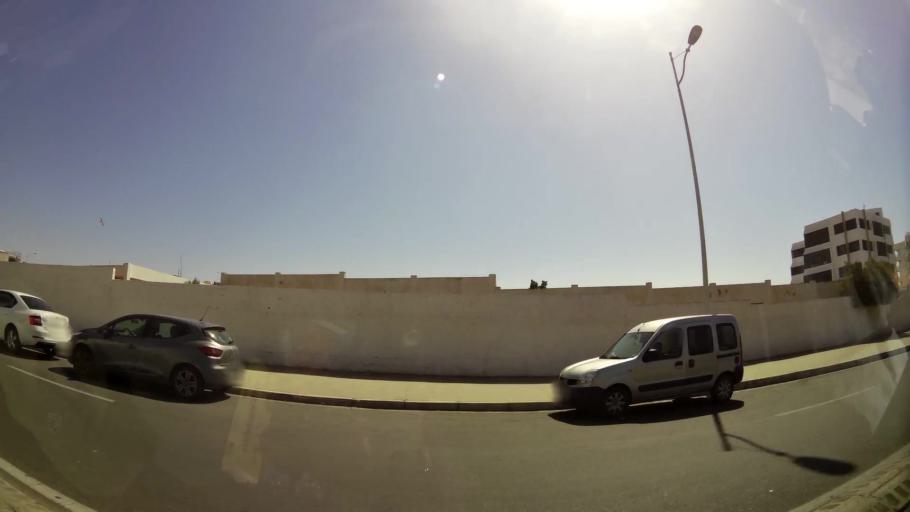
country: MA
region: Souss-Massa-Draa
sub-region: Agadir-Ida-ou-Tnan
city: Agadir
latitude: 30.4243
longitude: -9.5889
